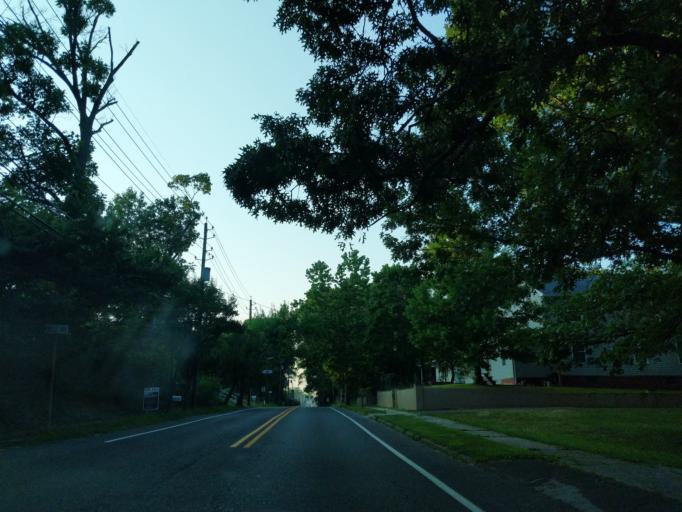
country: US
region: New Jersey
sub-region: Camden County
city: Glendora
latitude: 39.8214
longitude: -75.0991
